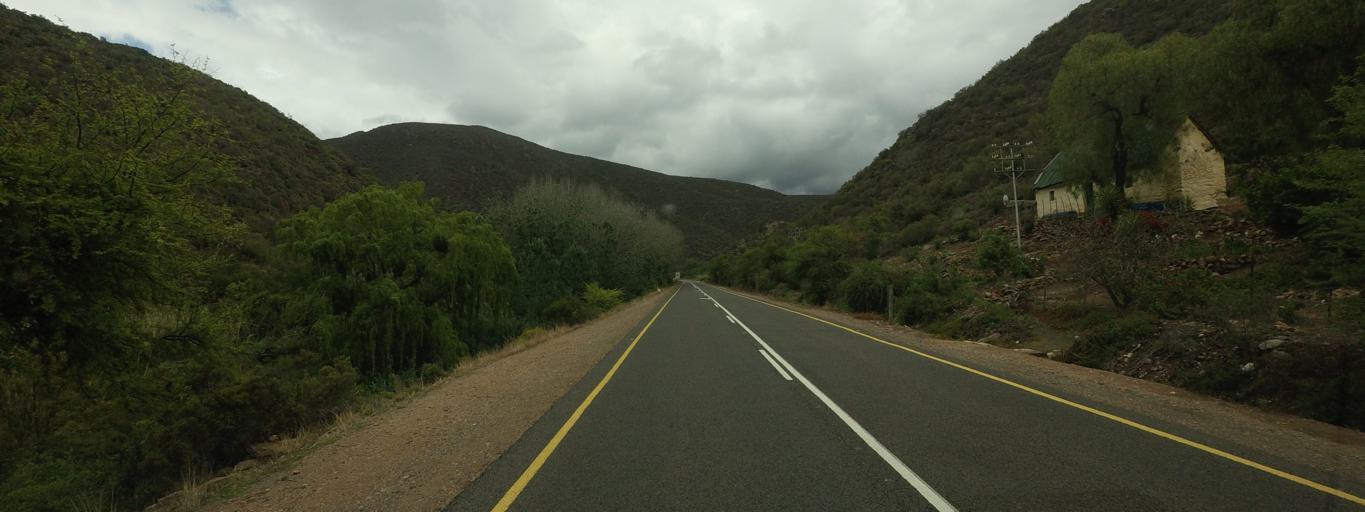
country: ZA
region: Western Cape
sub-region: Eden District Municipality
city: Oudtshoorn
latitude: -33.4660
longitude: 22.2553
